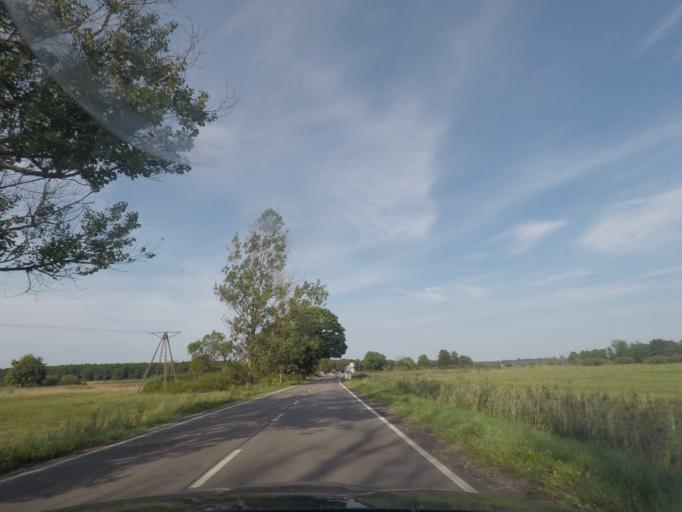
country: PL
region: Pomeranian Voivodeship
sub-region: Powiat leborski
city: Leba
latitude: 54.6535
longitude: 17.5625
